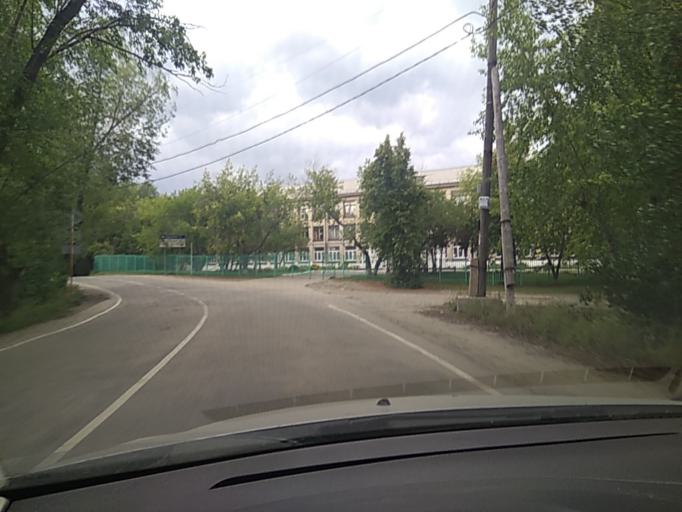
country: RU
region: Chelyabinsk
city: Kyshtym
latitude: 55.7023
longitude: 60.5308
